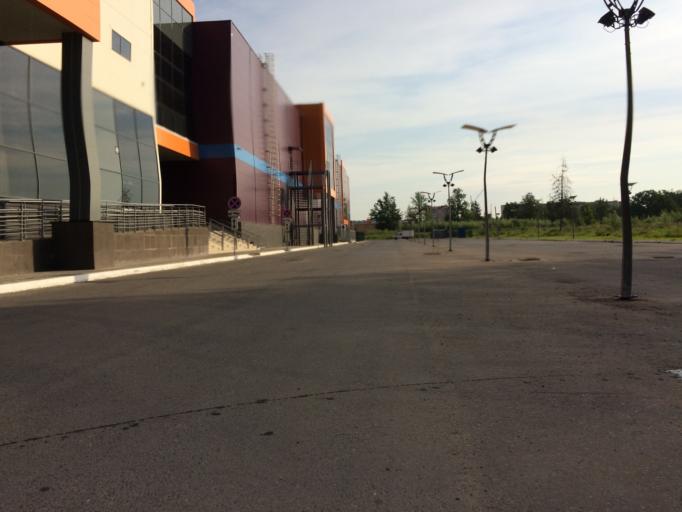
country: RU
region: Mariy-El
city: Yoshkar-Ola
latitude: 56.6272
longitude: 47.9306
